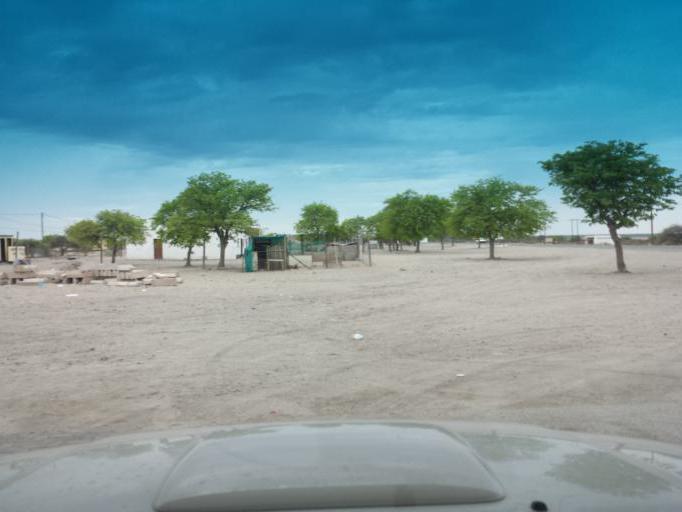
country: BW
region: Central
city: Mopipi
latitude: -21.2056
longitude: 24.8694
